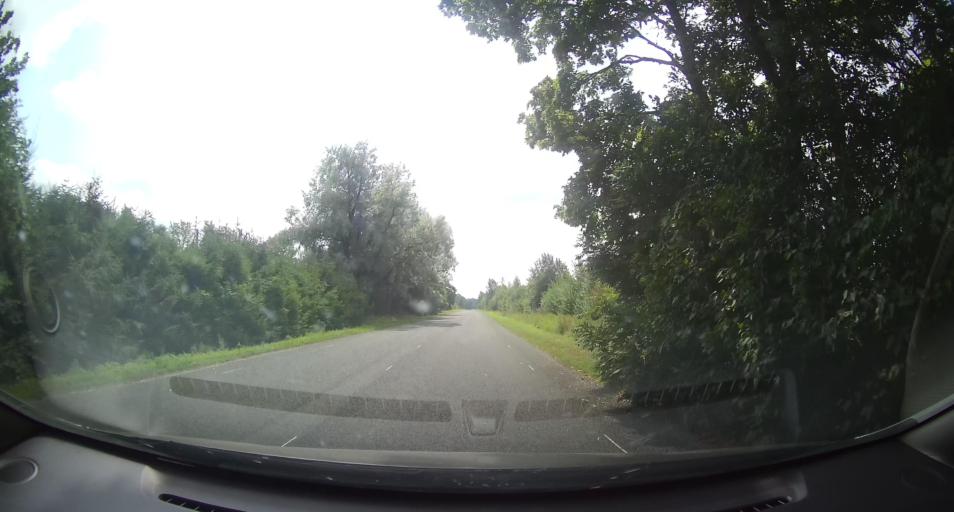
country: EE
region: Paernumaa
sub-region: Audru vald
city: Audru
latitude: 58.4926
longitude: 24.3357
